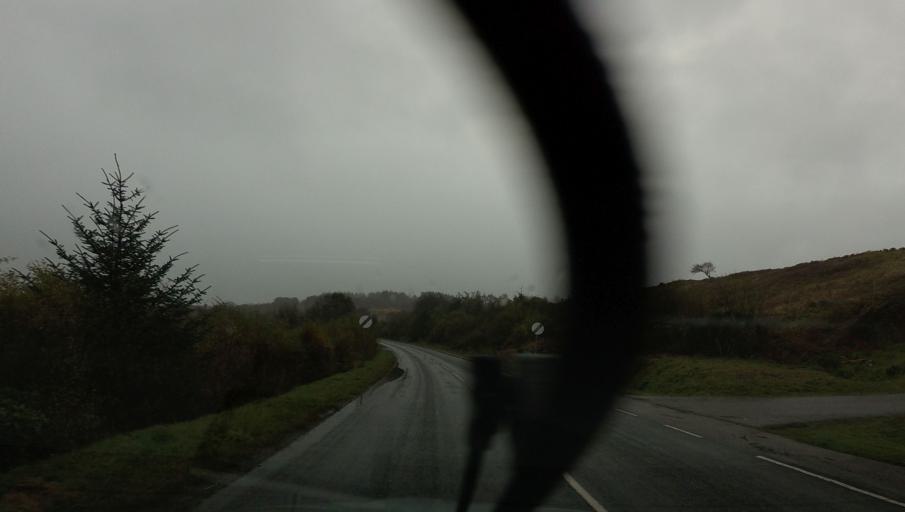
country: GB
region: Scotland
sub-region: Argyll and Bute
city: Isle Of Mull
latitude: 56.6138
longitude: -6.0696
